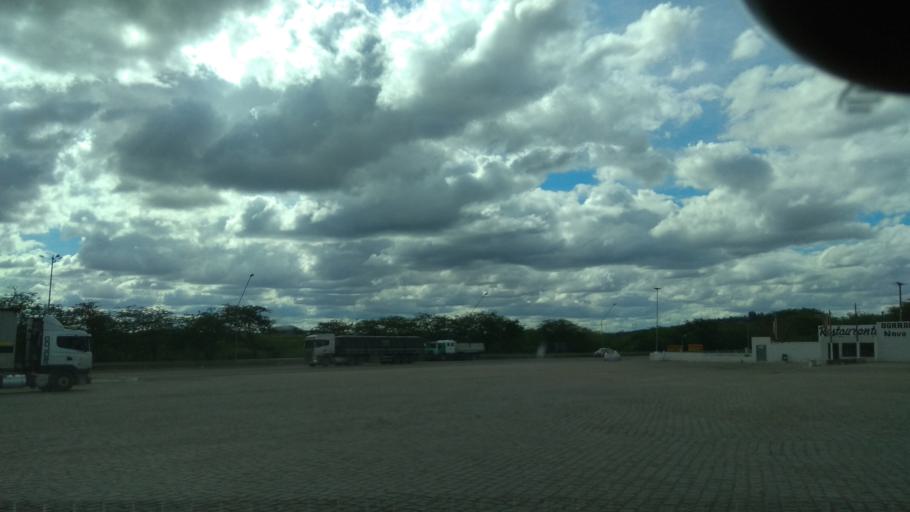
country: BR
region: Bahia
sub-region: Santa Ines
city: Santa Ines
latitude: -12.9829
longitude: -39.9413
